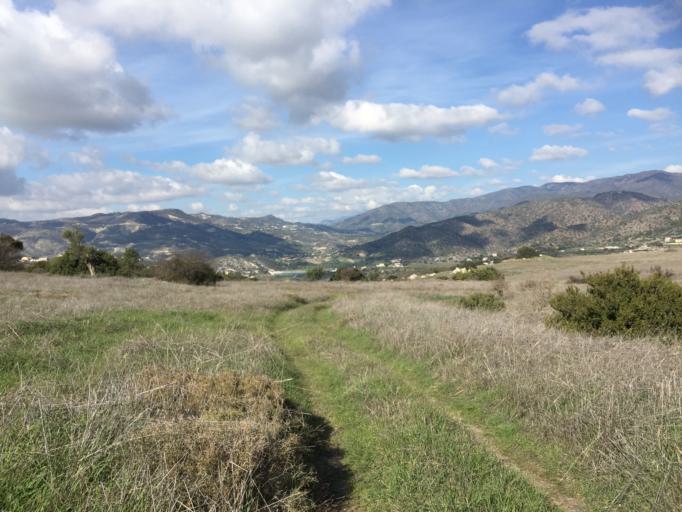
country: CY
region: Larnaka
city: Agios Tychon
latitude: 34.7465
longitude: 33.1173
